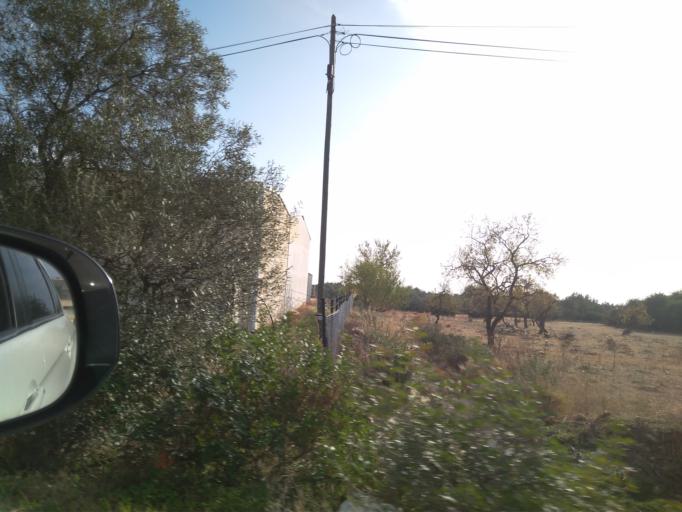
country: PT
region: Faro
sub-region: Faro
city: Santa Barbara de Nexe
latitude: 37.0945
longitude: -7.9470
